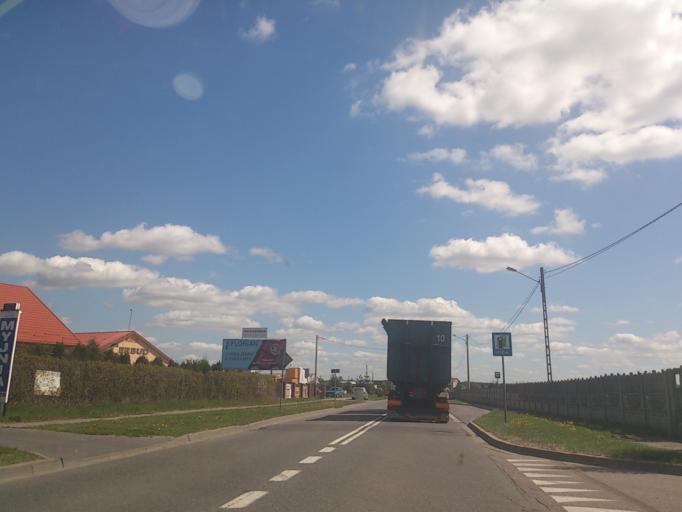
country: PL
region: Masovian Voivodeship
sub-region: Powiat makowski
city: Krasnosielc
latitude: 53.0343
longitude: 21.1685
